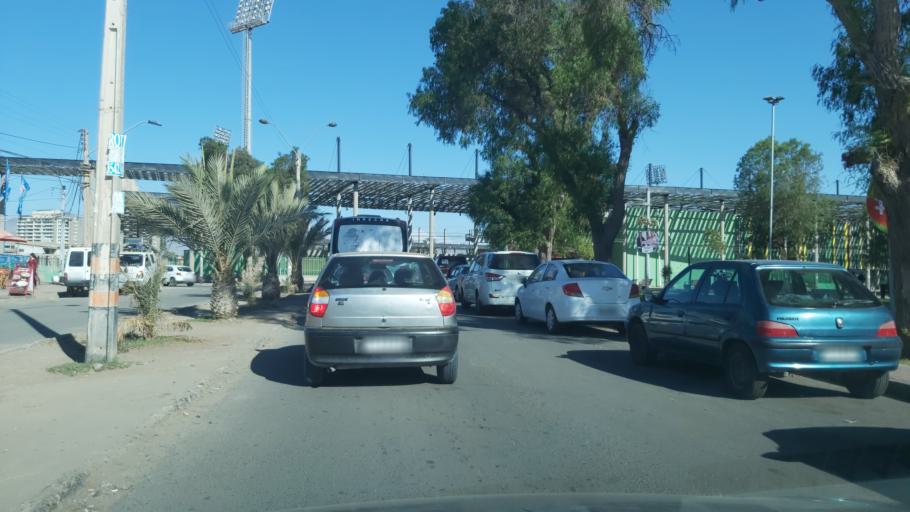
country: CL
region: Atacama
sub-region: Provincia de Copiapo
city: Copiapo
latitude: -27.3756
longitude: -70.3215
